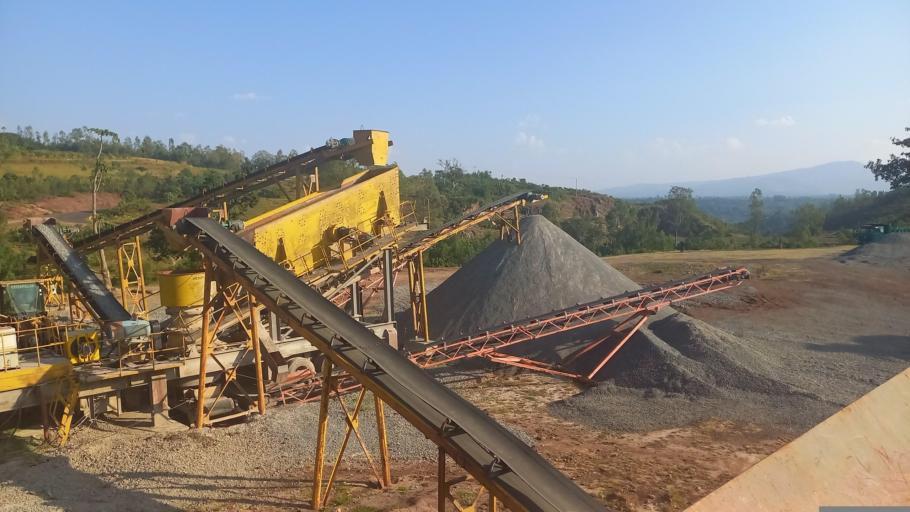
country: ET
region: Southern Nations, Nationalities, and People's Region
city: Areka
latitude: 7.2289
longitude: 37.5928
